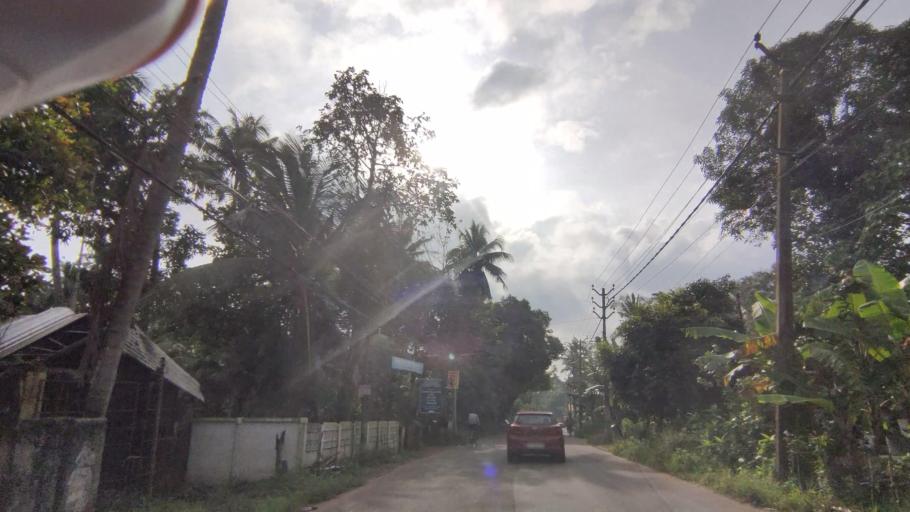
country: IN
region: Kerala
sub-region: Kottayam
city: Kottayam
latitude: 9.5940
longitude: 76.4790
